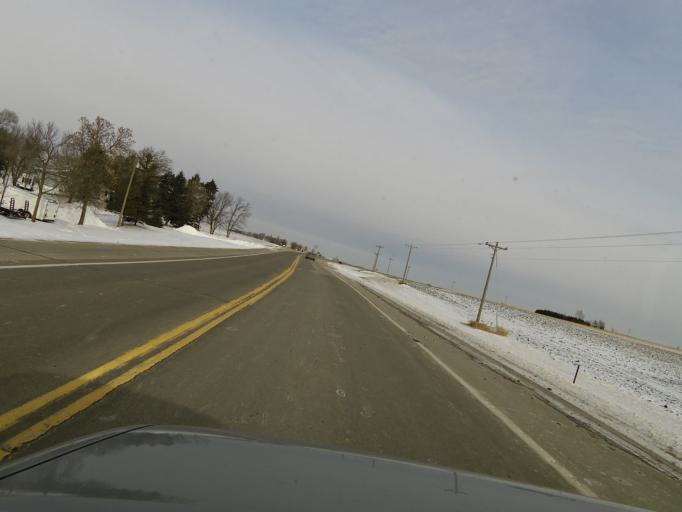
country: US
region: Minnesota
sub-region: Scott County
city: Jordan
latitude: 44.6771
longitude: -93.5722
